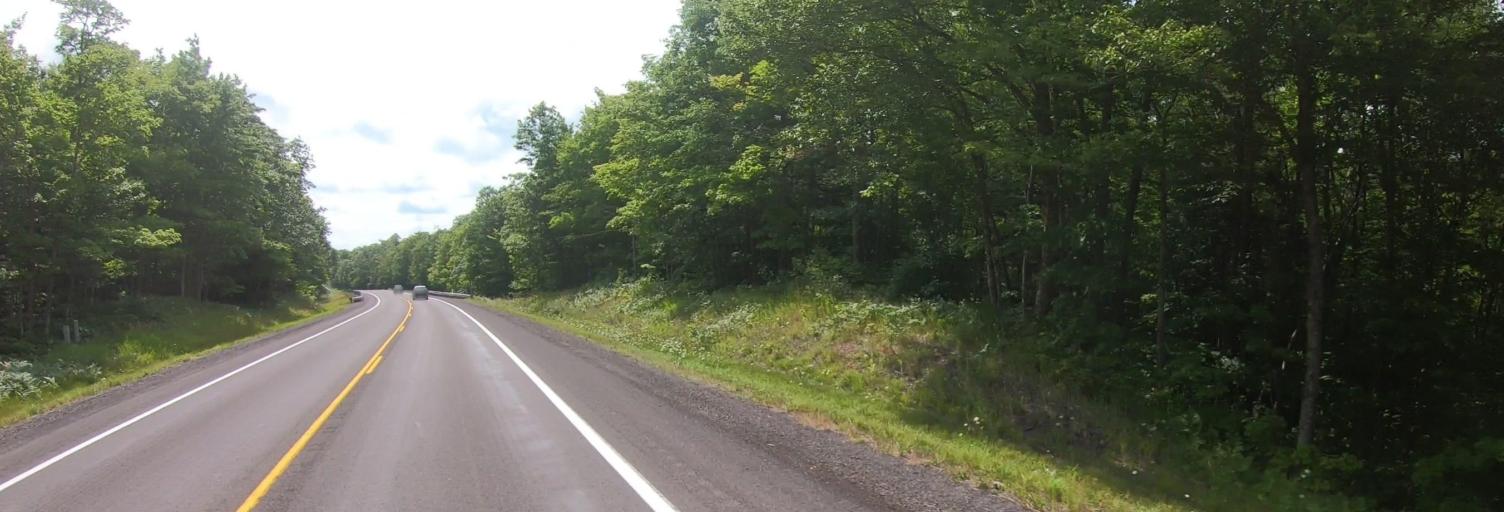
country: US
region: Michigan
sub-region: Houghton County
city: Hancock
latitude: 47.0366
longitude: -88.6824
